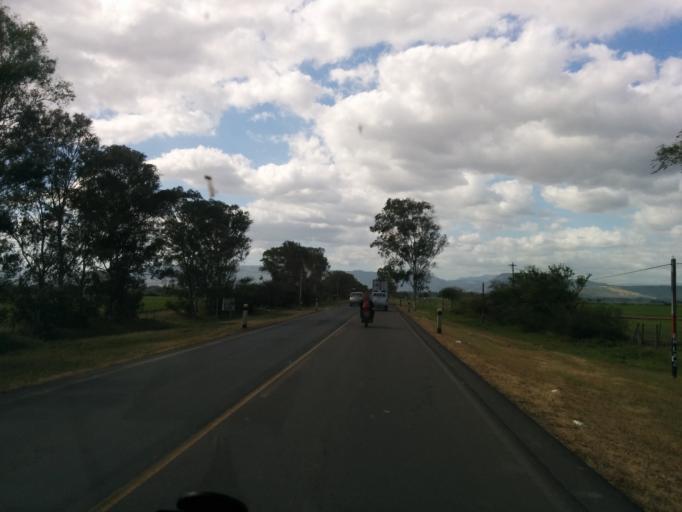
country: NI
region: Matagalpa
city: Ciudad Dario
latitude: 12.8650
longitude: -86.1144
